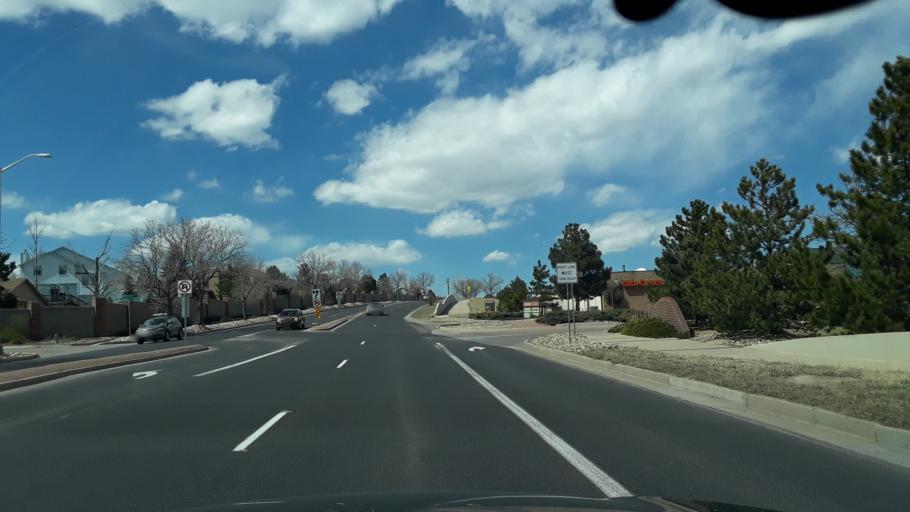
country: US
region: Colorado
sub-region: El Paso County
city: Black Forest
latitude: 38.9379
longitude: -104.7620
